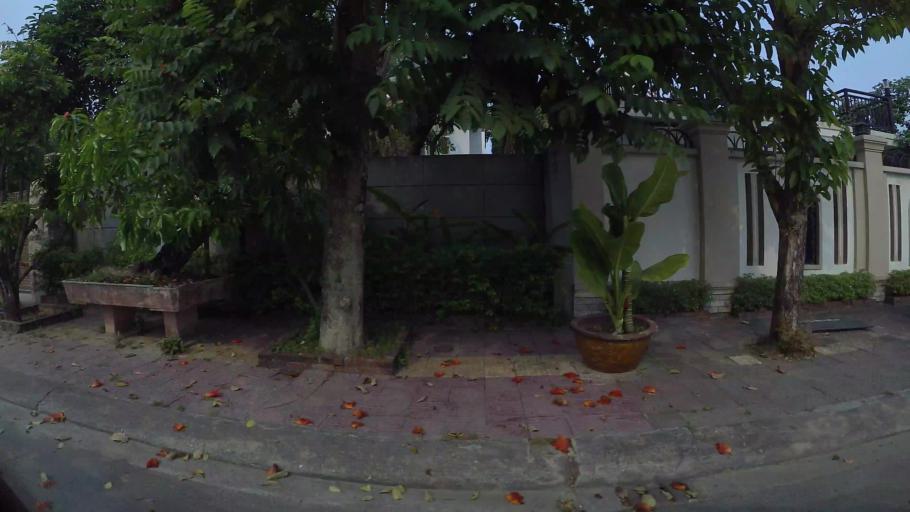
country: VN
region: Da Nang
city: Son Tra
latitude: 16.0458
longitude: 108.2269
